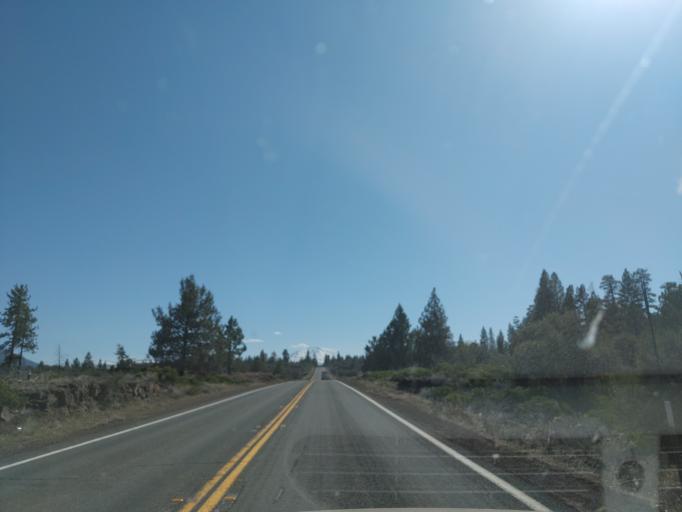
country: US
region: California
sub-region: Shasta County
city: Burney
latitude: 40.6935
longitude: -121.4189
